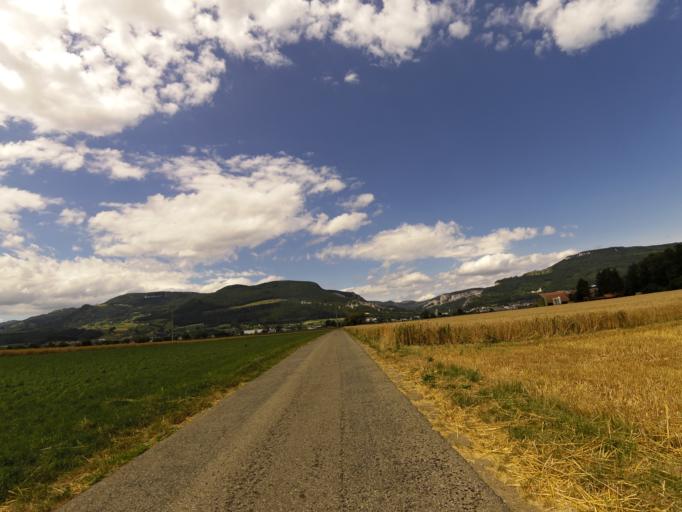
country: CH
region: Solothurn
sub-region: Bezirk Gaeu
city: Oensingen
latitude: 47.2647
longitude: 7.7240
